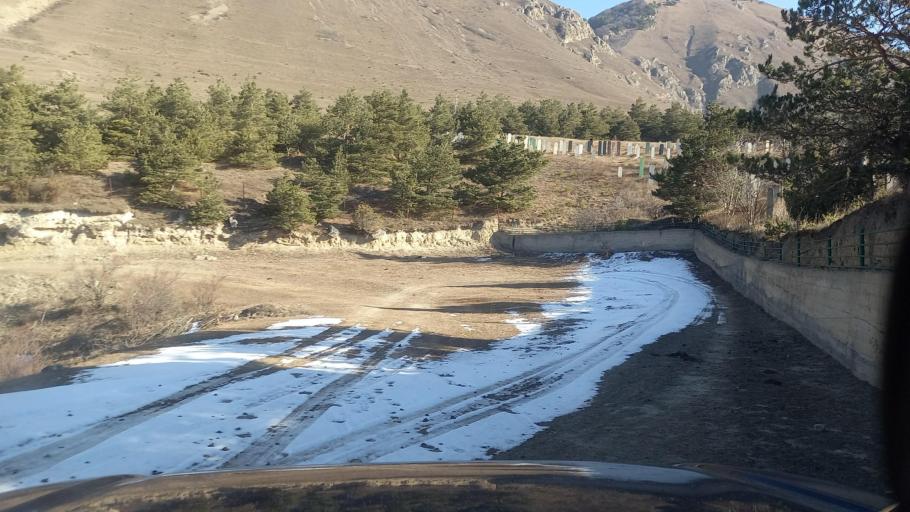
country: RU
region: Ingushetiya
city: Dzhayrakh
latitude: 42.8472
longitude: 44.6552
